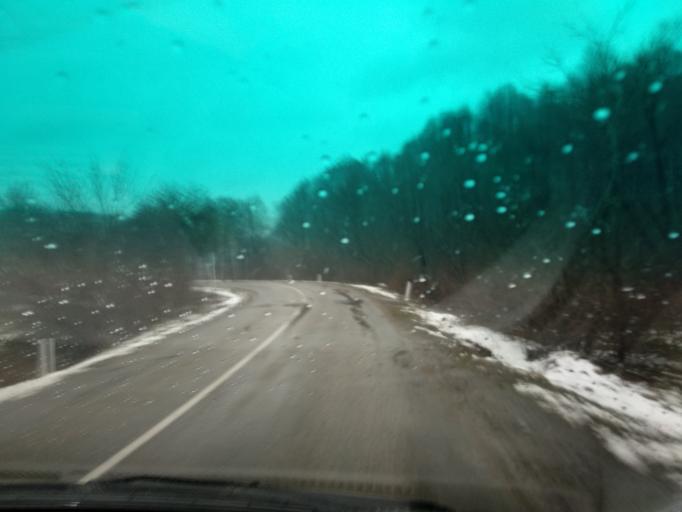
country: RU
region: Krasnodarskiy
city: Khadyzhensk
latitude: 44.2323
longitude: 39.3835
